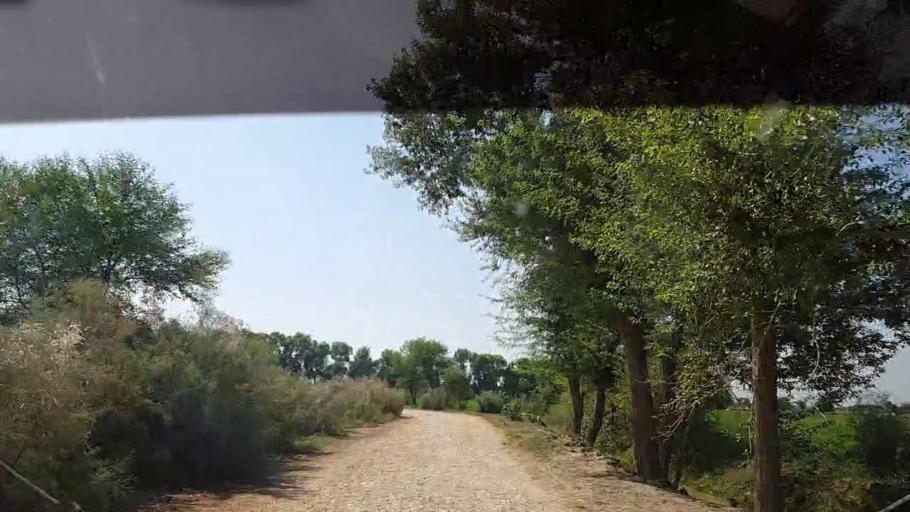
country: PK
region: Sindh
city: Ghauspur
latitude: 28.2128
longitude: 69.0858
